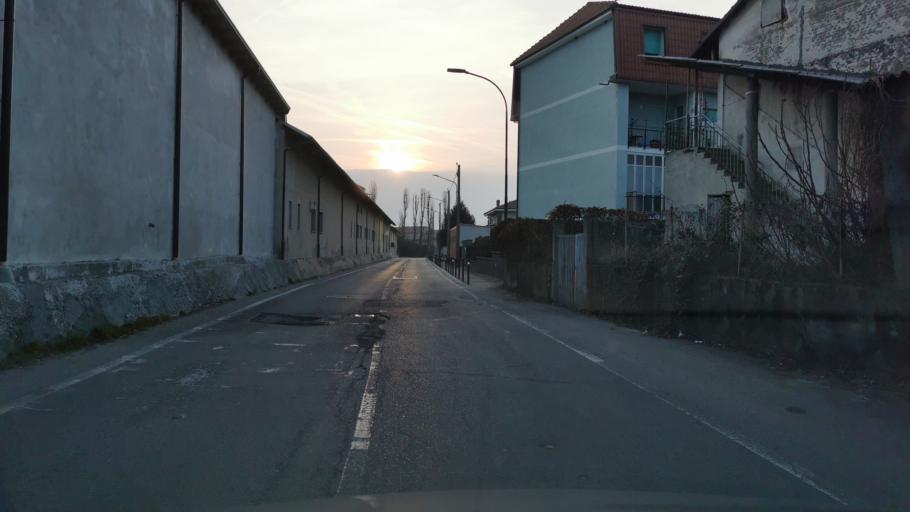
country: IT
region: Piedmont
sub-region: Provincia di Torino
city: Rivarolo Canavese
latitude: 45.3335
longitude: 7.7165
